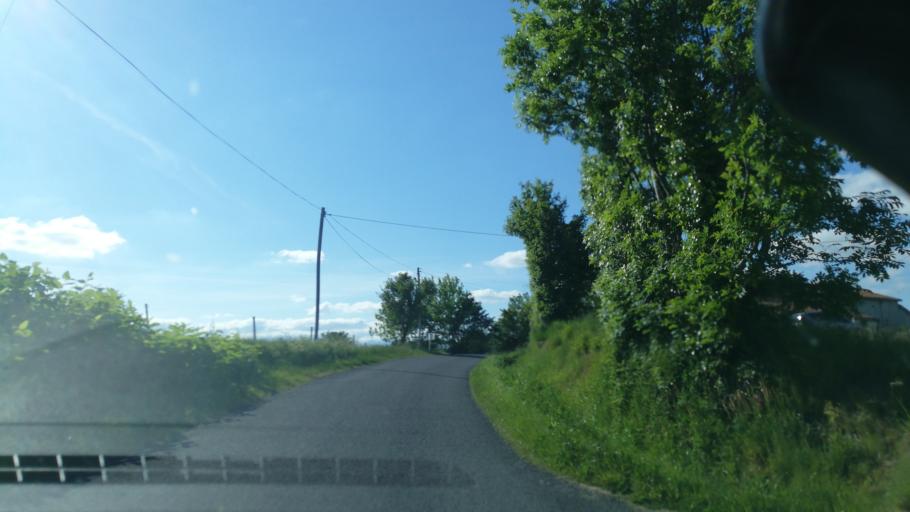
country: FR
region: Poitou-Charentes
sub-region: Departement des Deux-Sevres
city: Moncoutant
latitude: 46.7100
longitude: -0.5873
